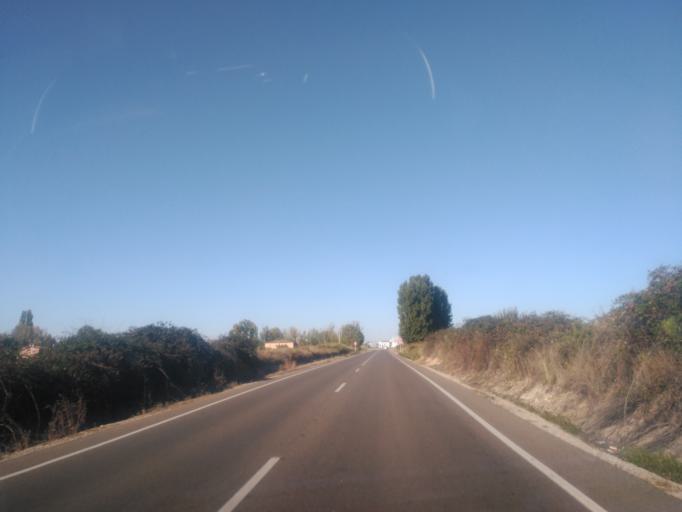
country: ES
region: Castille and Leon
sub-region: Provincia de Burgos
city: Fresnillo de las Duenas
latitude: 41.6761
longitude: -3.6550
